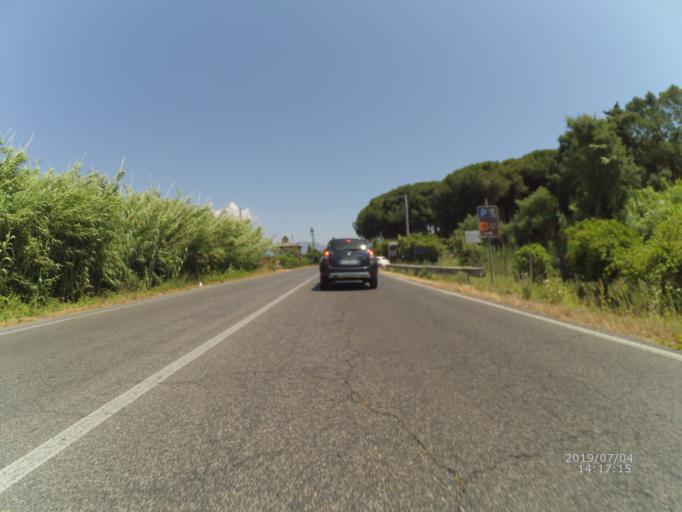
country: IT
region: Latium
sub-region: Provincia di Latina
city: Monte San Biagio
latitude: 41.2898
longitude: 13.3668
